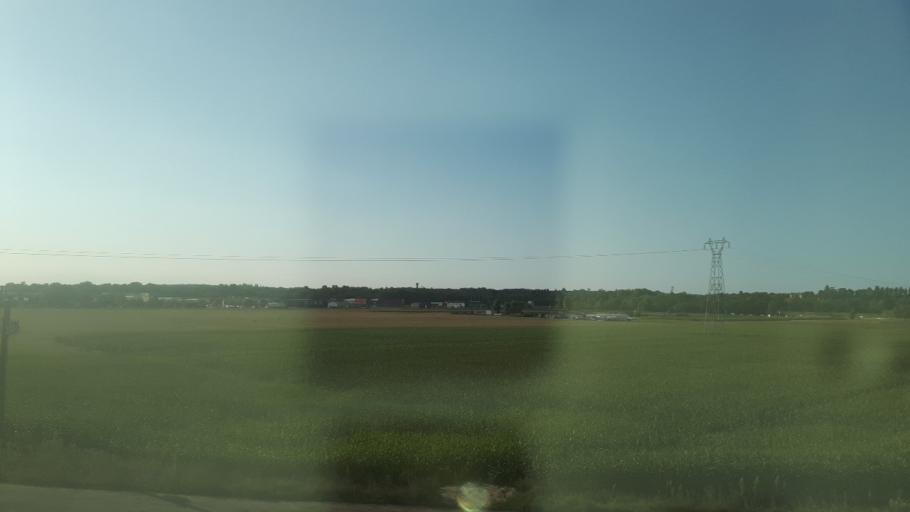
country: FR
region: Centre
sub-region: Departement d'Indre-et-Loire
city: Vouvray
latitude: 47.3936
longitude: 0.7959
